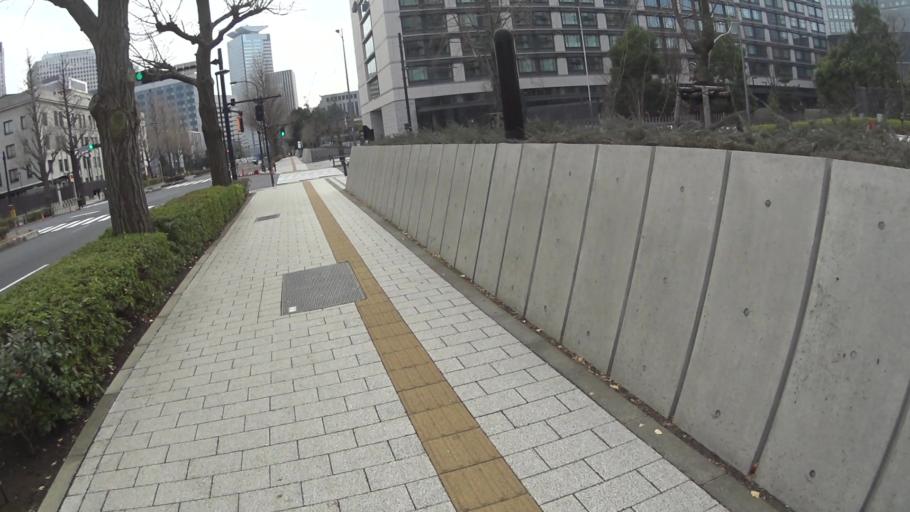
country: JP
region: Tokyo
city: Tokyo
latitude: 35.6743
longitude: 139.7442
